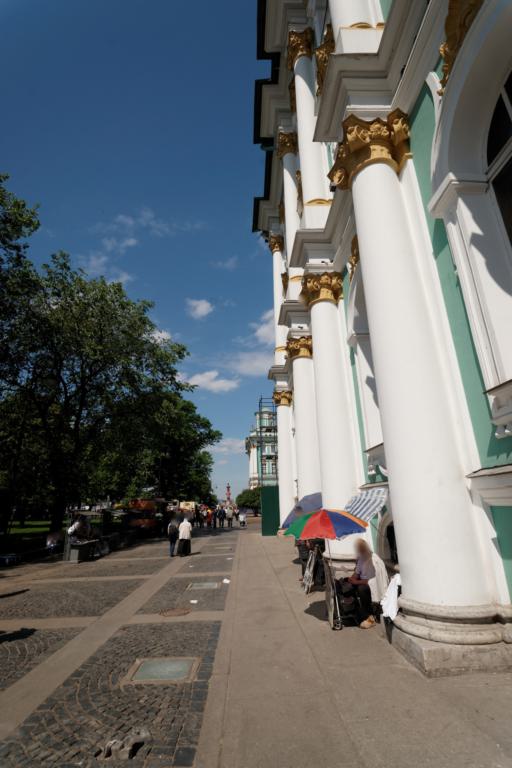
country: RU
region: St.-Petersburg
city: Saint Petersburg
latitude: 59.9392
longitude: 30.3131
